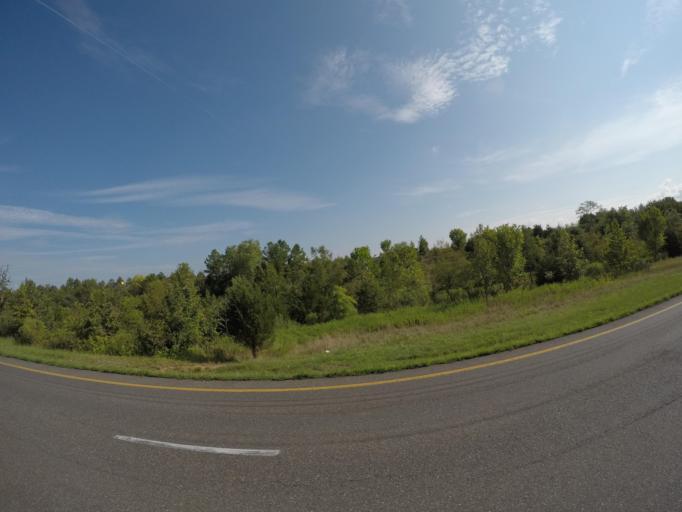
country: US
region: Maryland
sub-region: Anne Arundel County
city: Odenton
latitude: 39.1000
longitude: -76.6952
